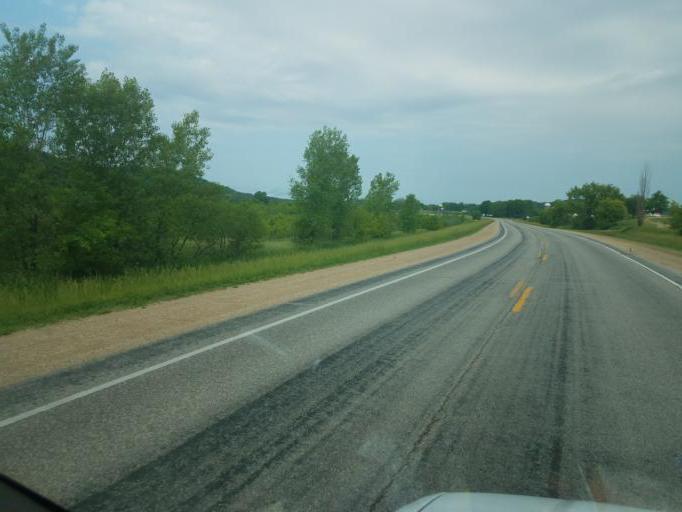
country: US
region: Wisconsin
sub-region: Vernon County
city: Hillsboro
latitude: 43.6580
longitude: -90.3688
